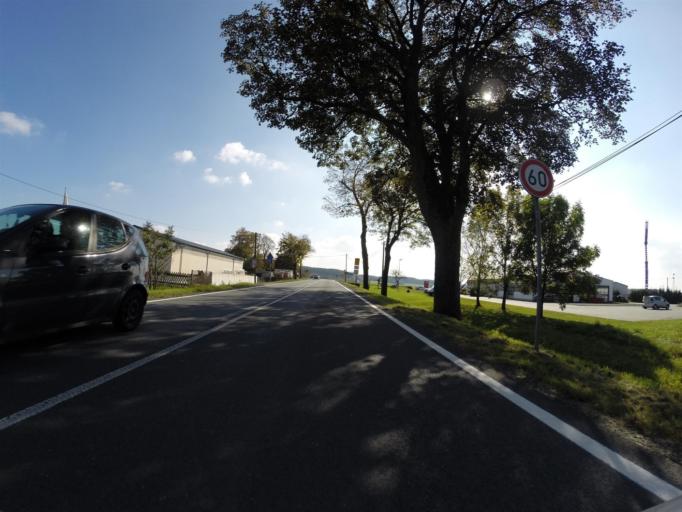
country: DE
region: Thuringia
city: Tanna
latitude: 50.4943
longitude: 11.8345
